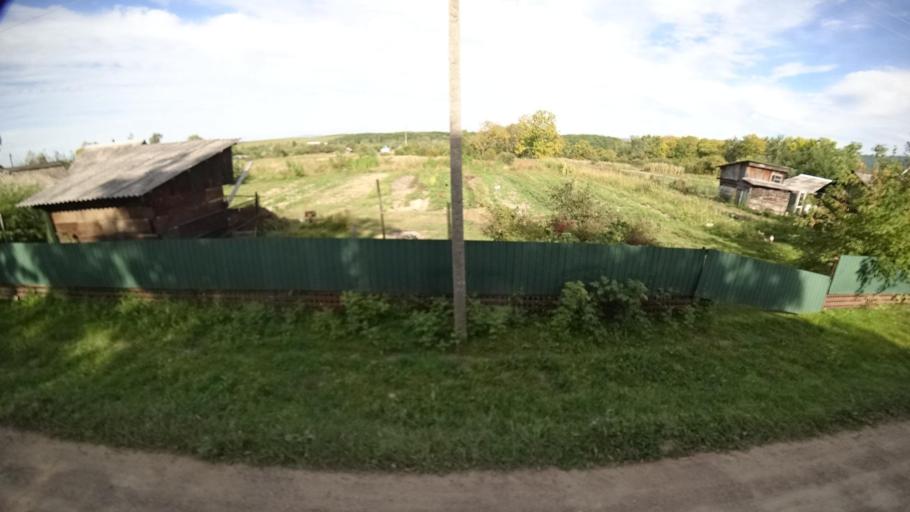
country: RU
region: Primorskiy
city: Dostoyevka
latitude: 44.3008
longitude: 133.4594
